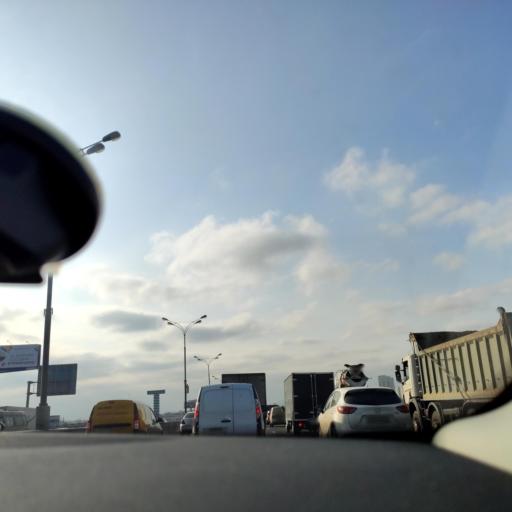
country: RU
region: Moskovskaya
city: Razvilka
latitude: 55.5854
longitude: 37.7100
